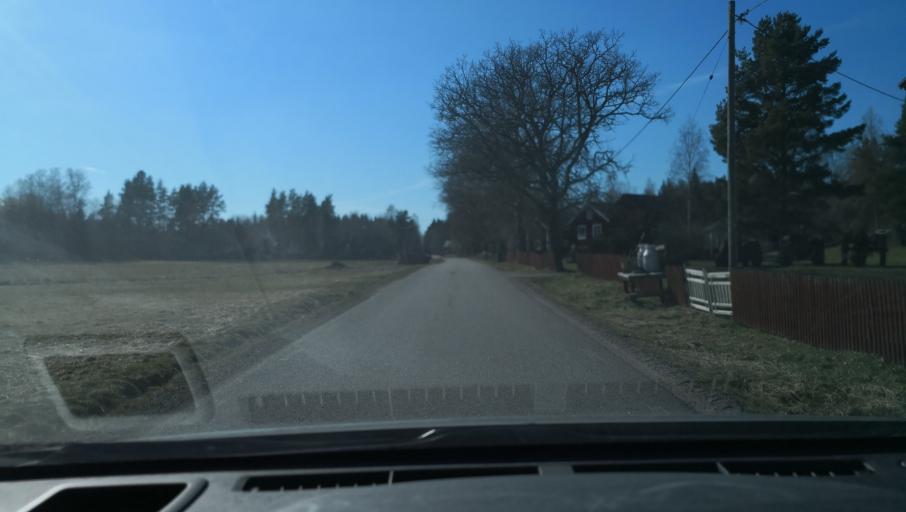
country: SE
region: Dalarna
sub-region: Avesta Kommun
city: Horndal
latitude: 60.0821
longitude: 16.4512
